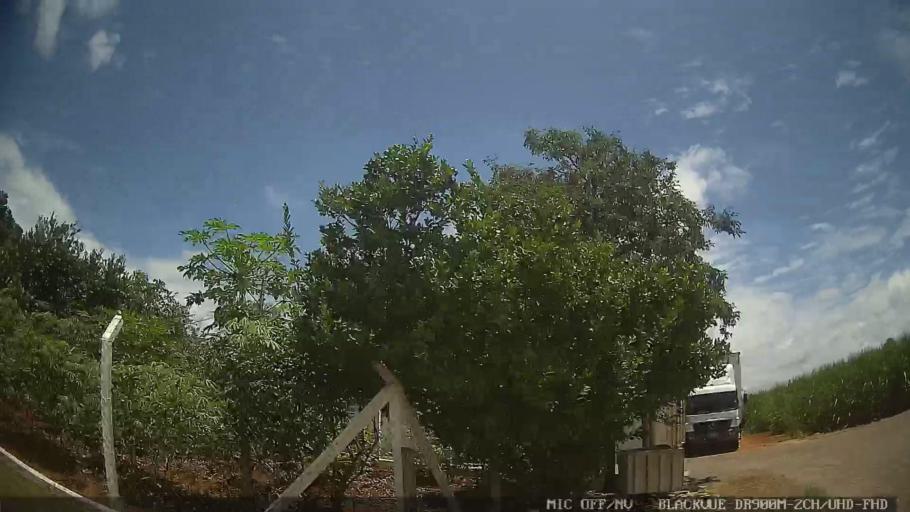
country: BR
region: Sao Paulo
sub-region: Laranjal Paulista
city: Laranjal Paulista
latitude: -23.0229
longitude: -47.8570
